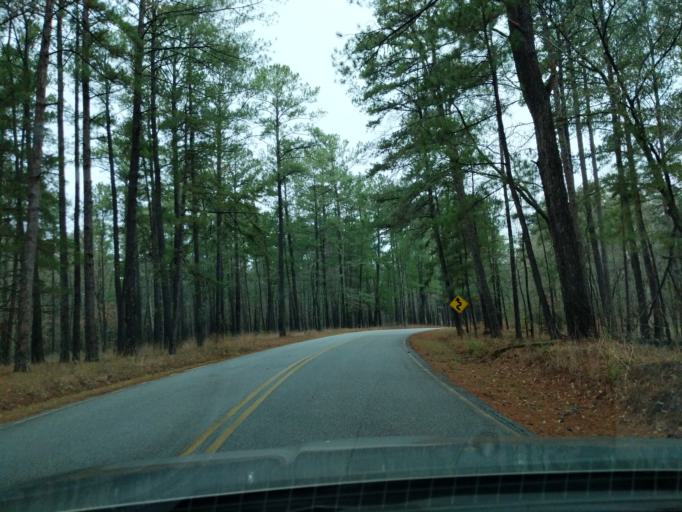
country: US
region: Georgia
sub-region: Columbia County
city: Appling
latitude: 33.6495
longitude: -82.3754
